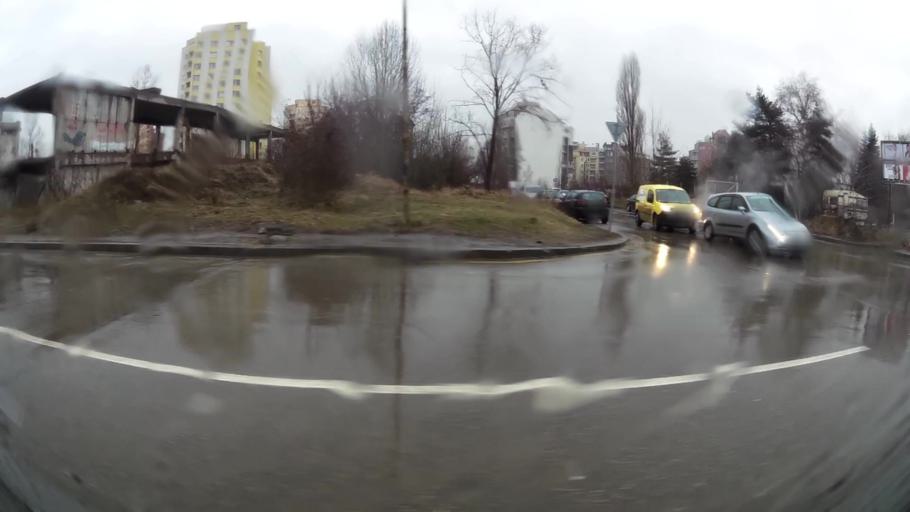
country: BG
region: Sofia-Capital
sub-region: Stolichna Obshtina
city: Sofia
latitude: 42.6464
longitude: 23.3422
